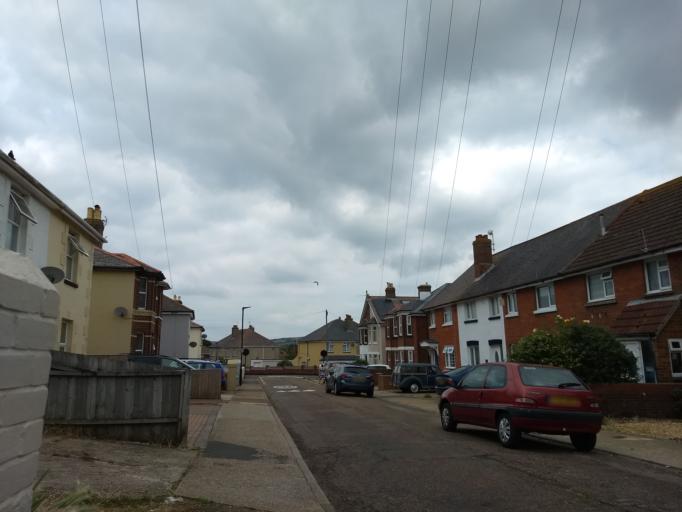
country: GB
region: England
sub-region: Isle of Wight
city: Sandown
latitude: 50.6487
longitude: -1.1716
